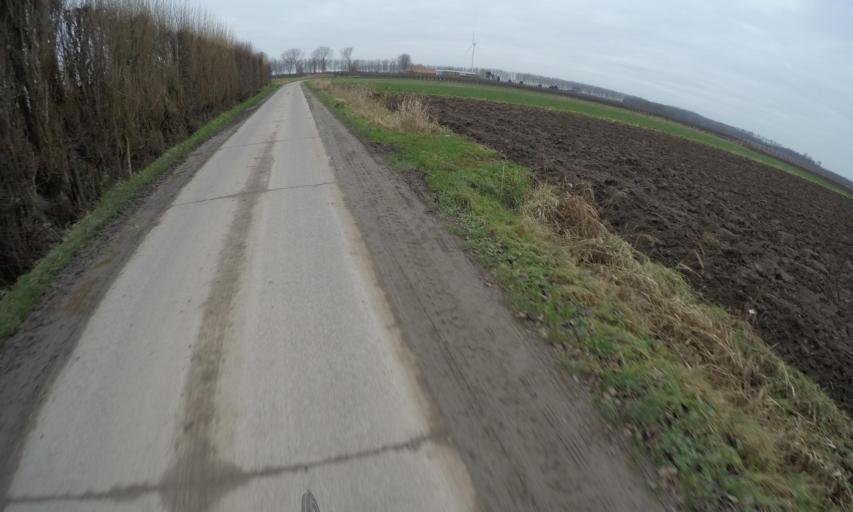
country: BE
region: Flanders
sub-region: Provincie Oost-Vlaanderen
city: Beveren
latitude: 51.2312
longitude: 4.2170
